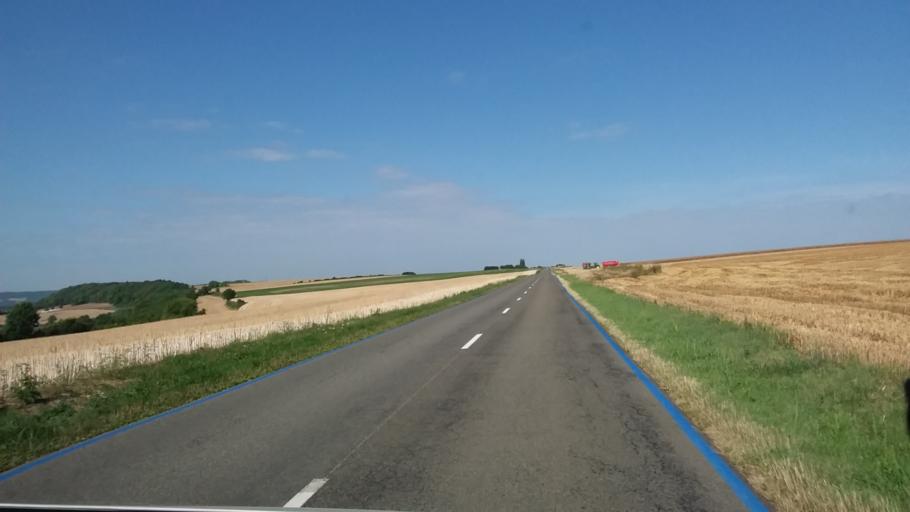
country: FR
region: Picardie
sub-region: Departement de l'Aisne
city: Bruyeres-et-Montberault
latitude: 49.4410
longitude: 3.6906
